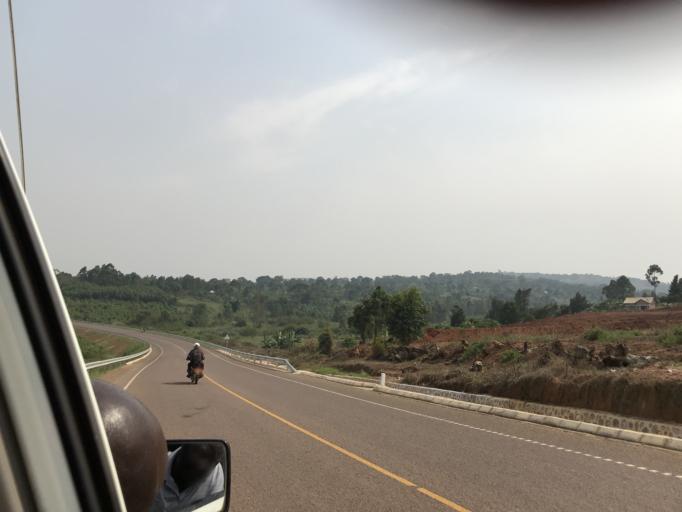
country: UG
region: Central Region
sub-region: Kalungu District
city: Kalungu
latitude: -0.2199
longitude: 31.7034
